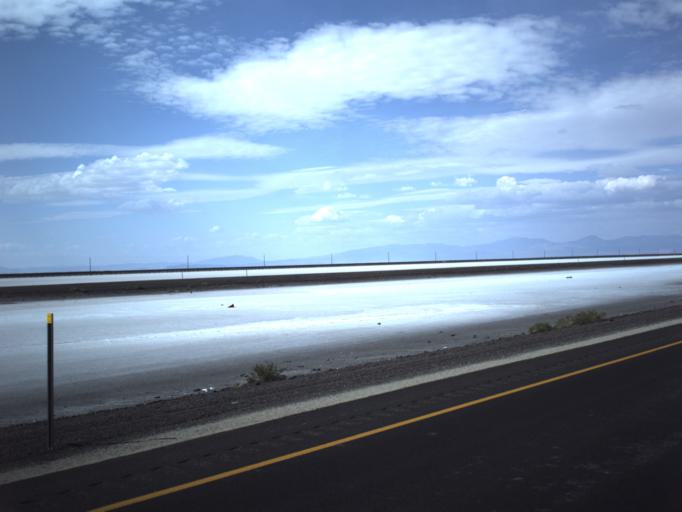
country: US
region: Utah
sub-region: Tooele County
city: Wendover
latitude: 40.7348
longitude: -113.6308
